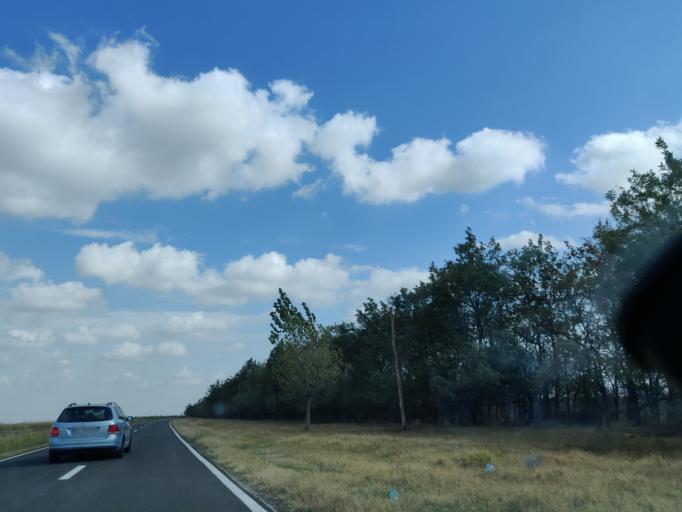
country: RO
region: Vrancea
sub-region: Comuna Maicanesti
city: Ramniceni
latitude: 45.4754
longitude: 27.4341
